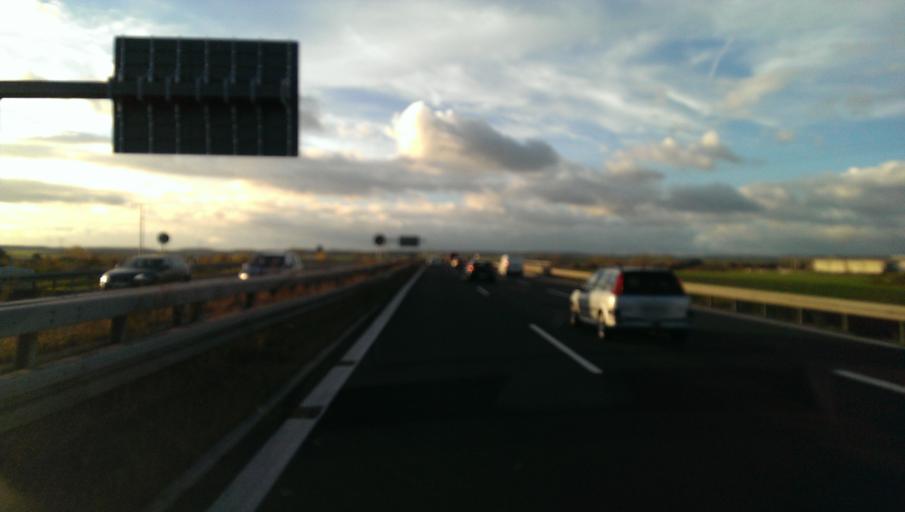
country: DE
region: Bavaria
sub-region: Regierungsbezirk Unterfranken
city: Bergrheinfeld
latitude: 50.0202
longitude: 10.1620
